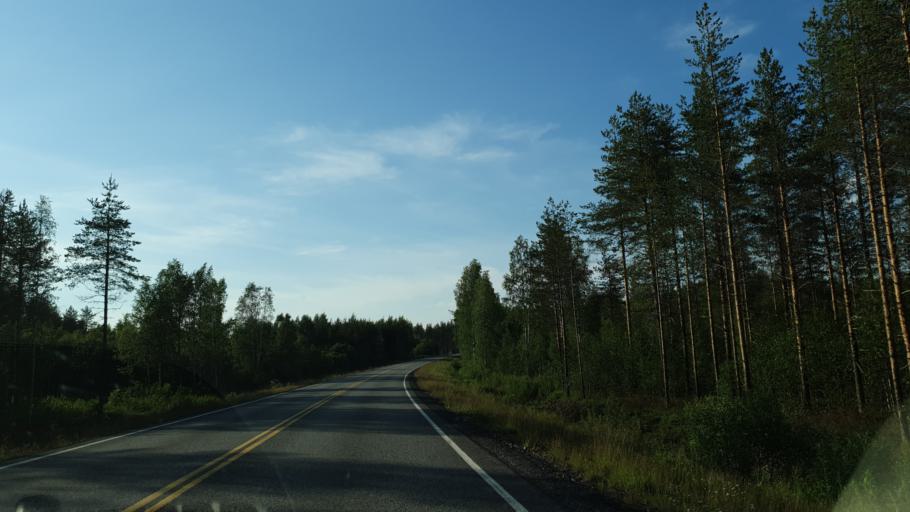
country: FI
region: Kainuu
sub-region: Kehys-Kainuu
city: Kuhmo
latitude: 64.0780
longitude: 29.4879
